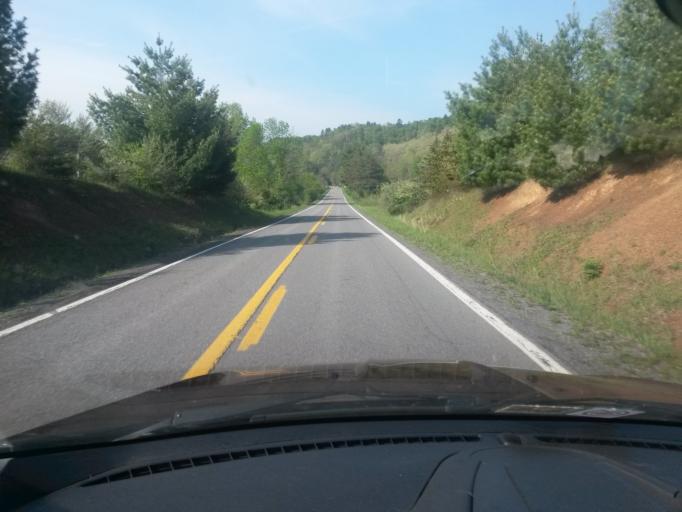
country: US
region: West Virginia
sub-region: Pocahontas County
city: Marlinton
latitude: 38.0330
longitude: -80.0365
